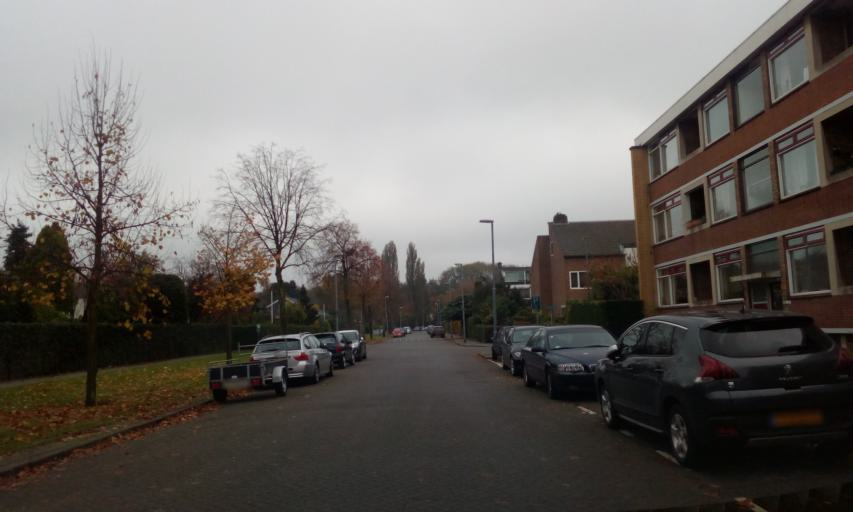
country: NL
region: South Holland
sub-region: Gemeente Lansingerland
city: Bergschenhoek
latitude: 51.9603
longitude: 4.5115
